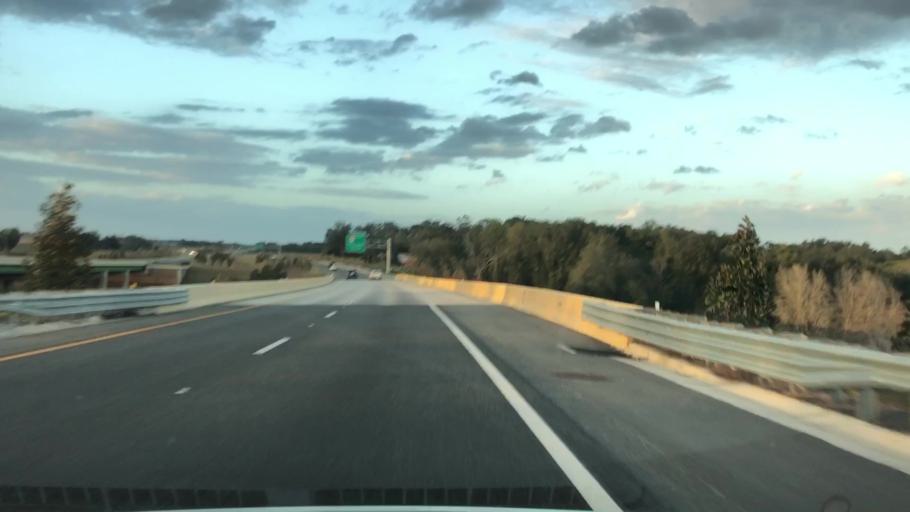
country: US
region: Florida
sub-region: Orange County
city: Zellwood
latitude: 28.7318
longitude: -81.5632
